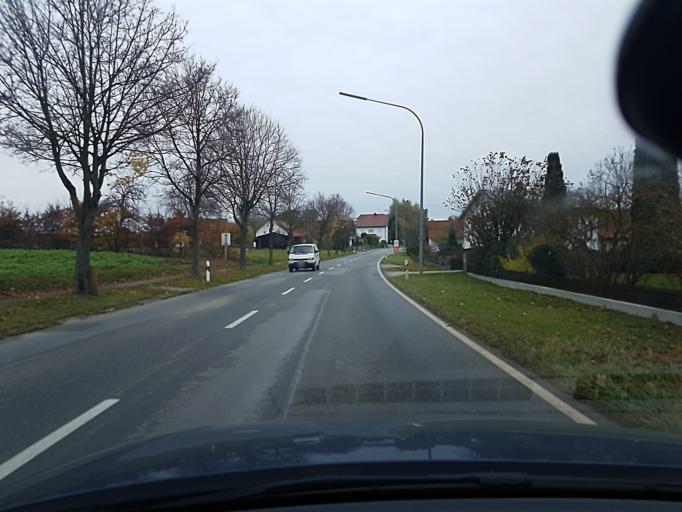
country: DE
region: Bavaria
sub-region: Lower Bavaria
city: Mallersdorf-Pfaffenberg
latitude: 48.7853
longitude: 12.1790
